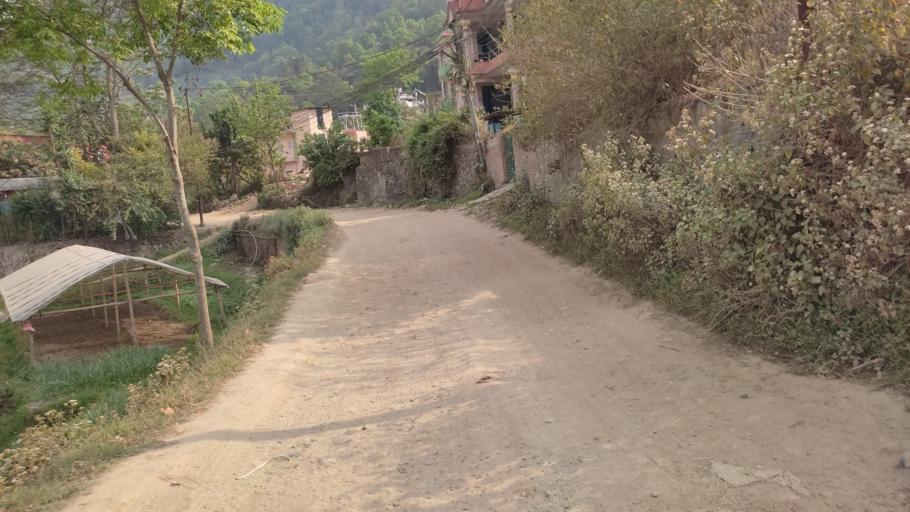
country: NP
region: Central Region
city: Kirtipur
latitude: 27.6640
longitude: 85.2579
